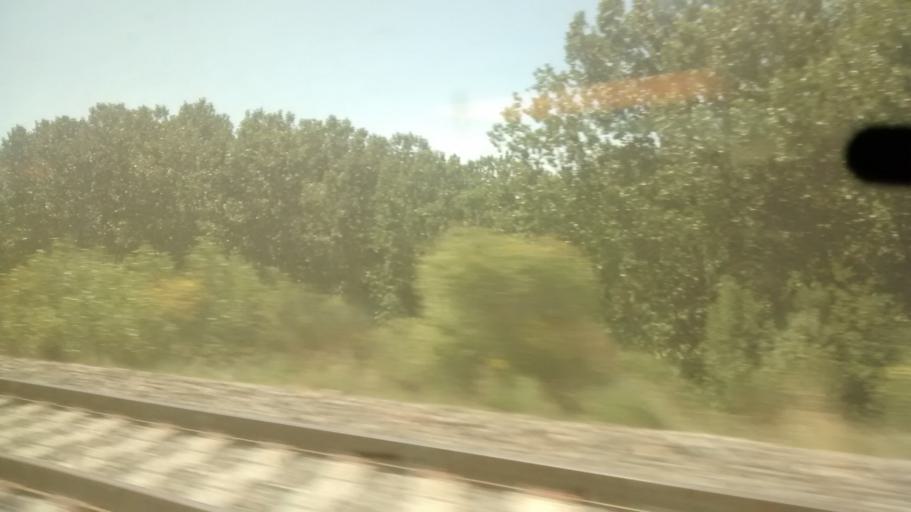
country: FR
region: Languedoc-Roussillon
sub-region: Departement du Gard
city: Montfaucon
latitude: 44.0767
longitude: 4.7674
